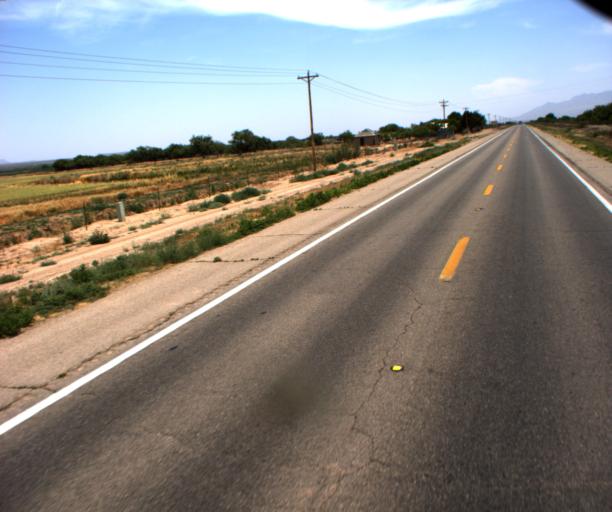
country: US
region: Arizona
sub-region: Graham County
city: Pima
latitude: 33.0139
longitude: -109.9510
